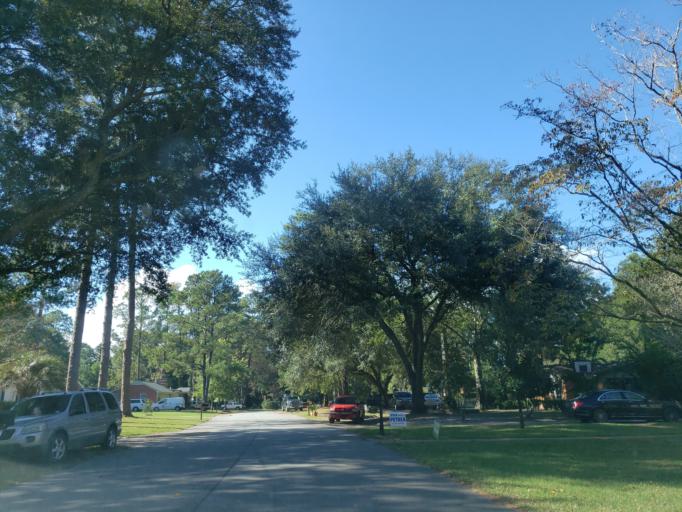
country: US
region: Georgia
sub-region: Chatham County
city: Isle of Hope
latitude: 31.9752
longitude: -81.0609
